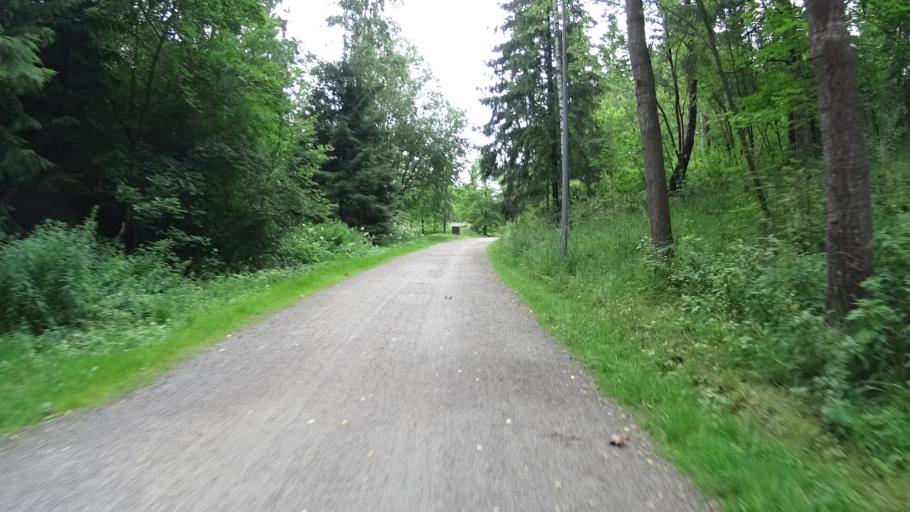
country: FI
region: Uusimaa
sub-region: Helsinki
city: Teekkarikylae
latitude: 60.2047
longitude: 24.8624
